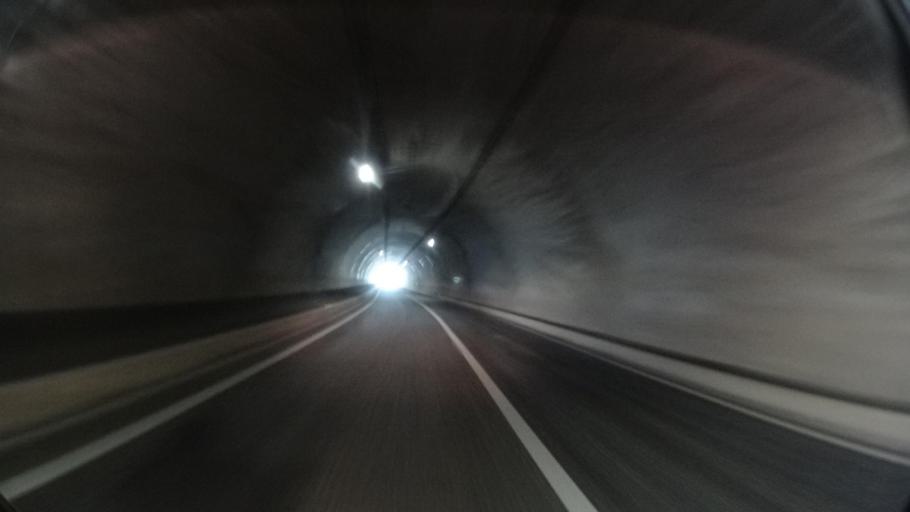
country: JP
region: Kyoto
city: Maizuru
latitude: 35.5348
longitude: 135.3475
